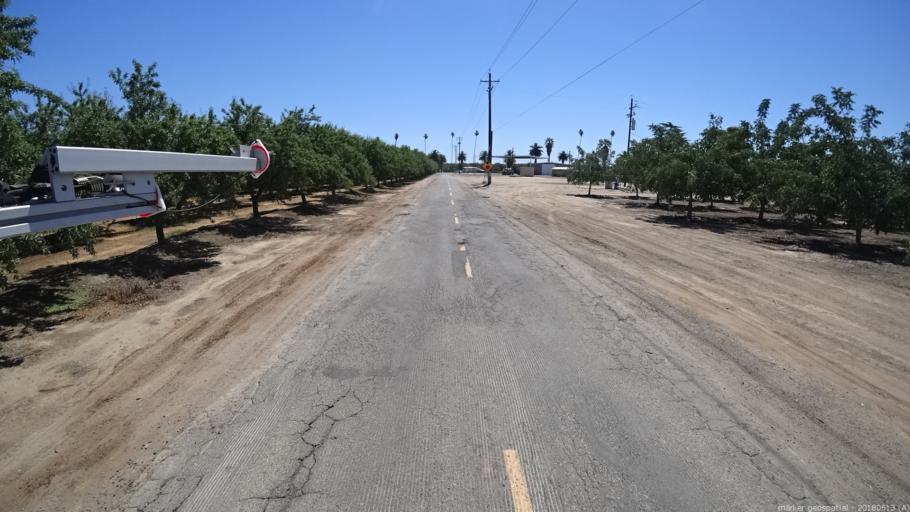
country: US
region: California
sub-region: Madera County
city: Chowchilla
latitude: 37.0617
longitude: -120.3183
